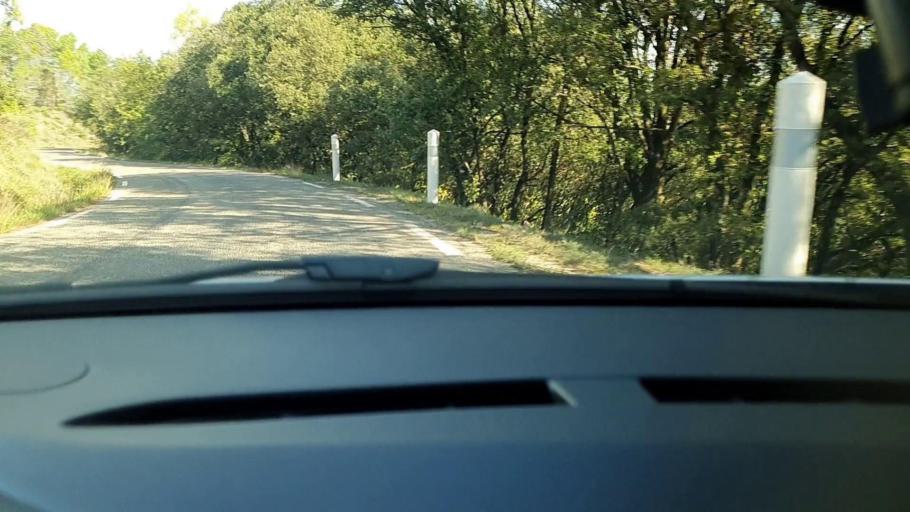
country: FR
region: Languedoc-Roussillon
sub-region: Departement du Gard
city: Saint-Florent-sur-Auzonnet
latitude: 44.2479
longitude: 4.1331
